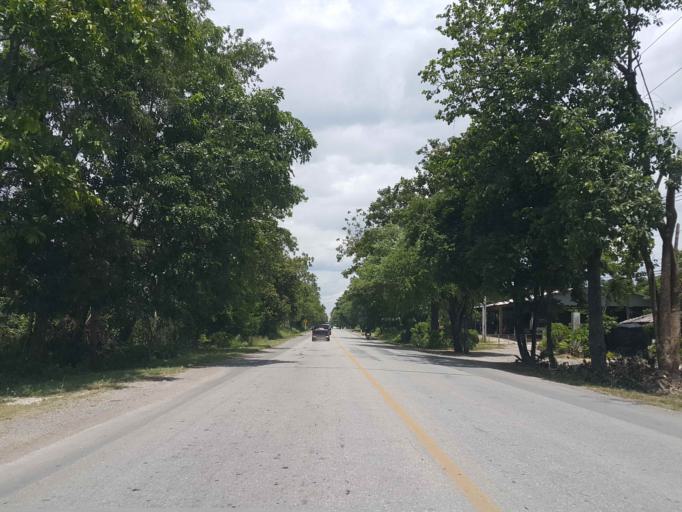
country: TH
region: Lamphun
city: Ban Hong
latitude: 18.3862
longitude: 98.8212
